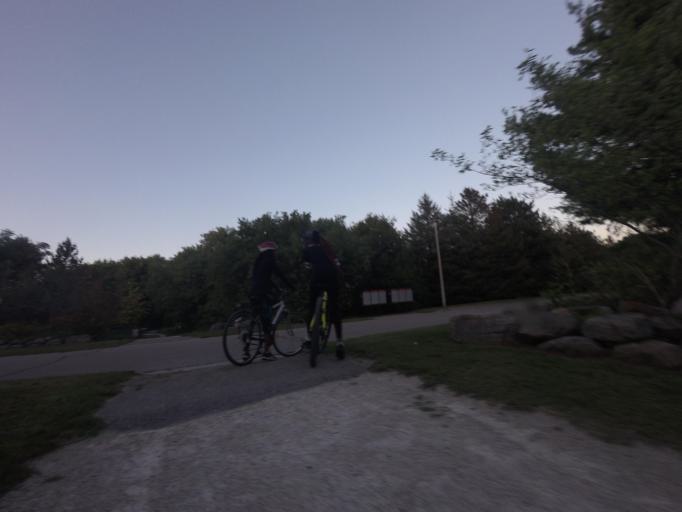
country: CA
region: Ontario
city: Orangeville
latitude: 43.9456
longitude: -79.8371
